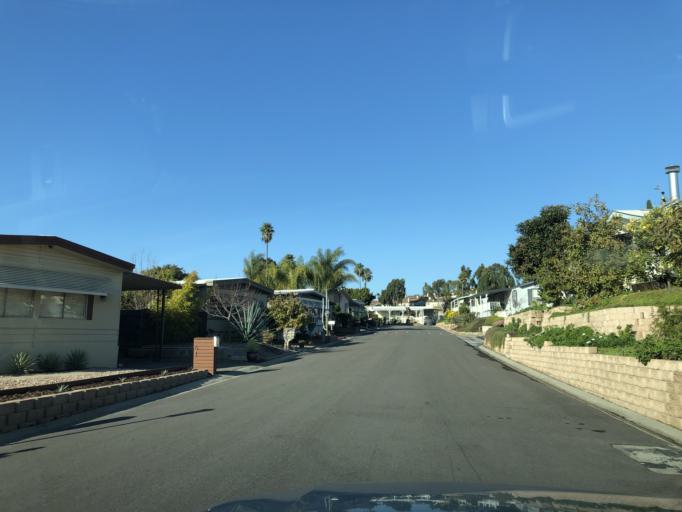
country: US
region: California
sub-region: San Diego County
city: Escondido
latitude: 33.1337
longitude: -117.0995
